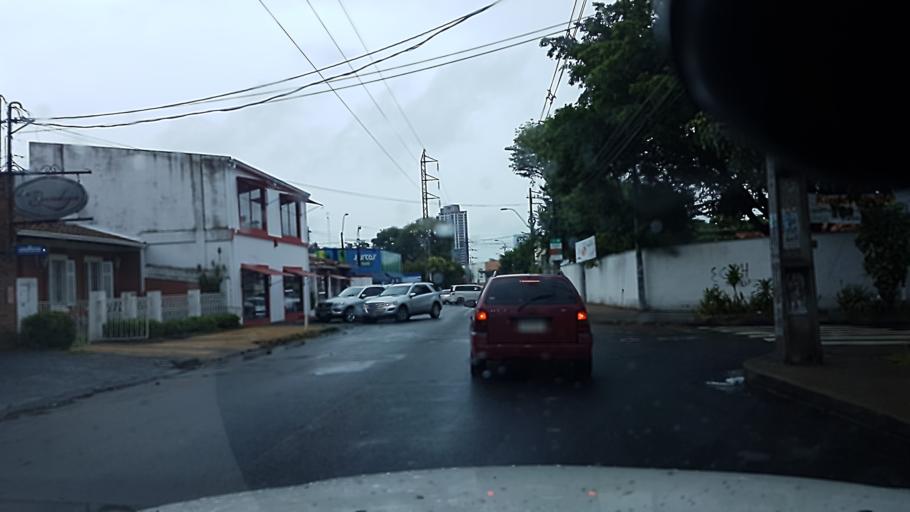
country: PY
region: Central
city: Fernando de la Mora
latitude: -25.2943
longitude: -57.5611
